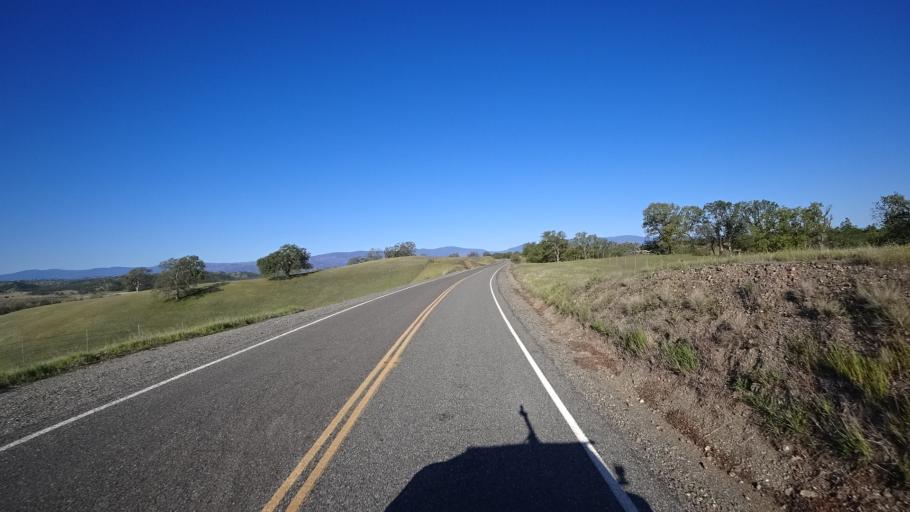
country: US
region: California
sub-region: Tehama County
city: Rancho Tehama Reserve
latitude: 39.8118
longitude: -122.3953
